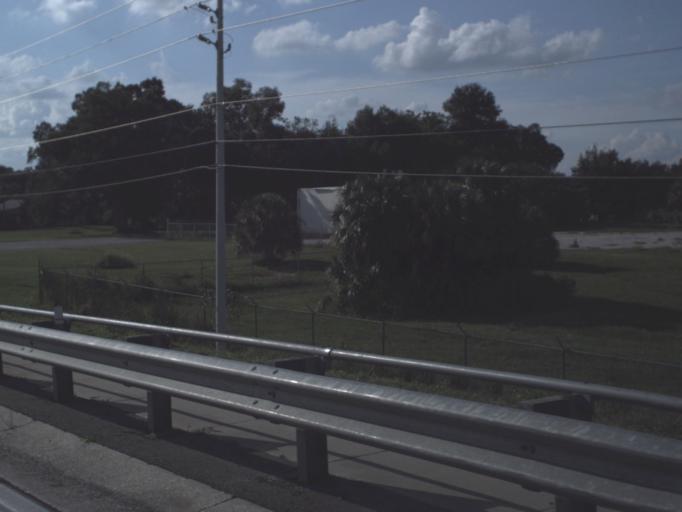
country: US
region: Florida
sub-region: Polk County
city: Lakeland
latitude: 28.0549
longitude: -81.9727
